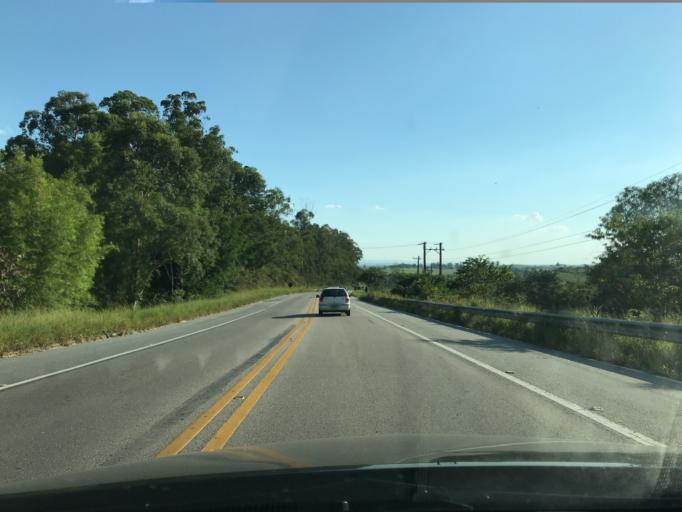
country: BR
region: Sao Paulo
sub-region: Tremembe
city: Tremembe
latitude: -22.9157
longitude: -45.5915
